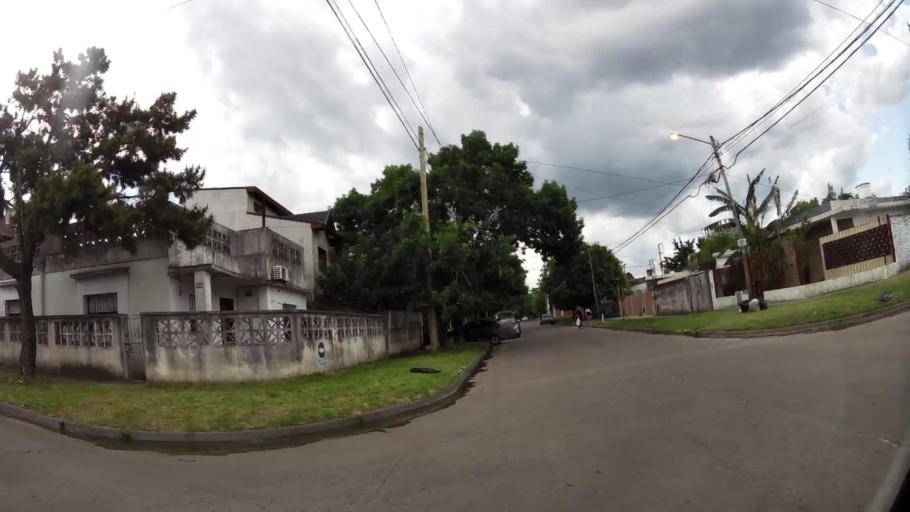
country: AR
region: Buenos Aires
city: Ituzaingo
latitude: -34.6374
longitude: -58.6851
